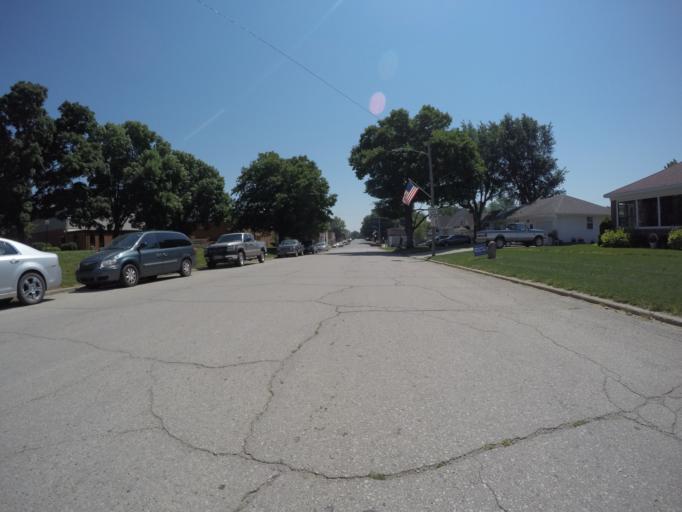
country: US
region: Kansas
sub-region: Doniphan County
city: Highland
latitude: 39.8595
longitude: -95.2709
